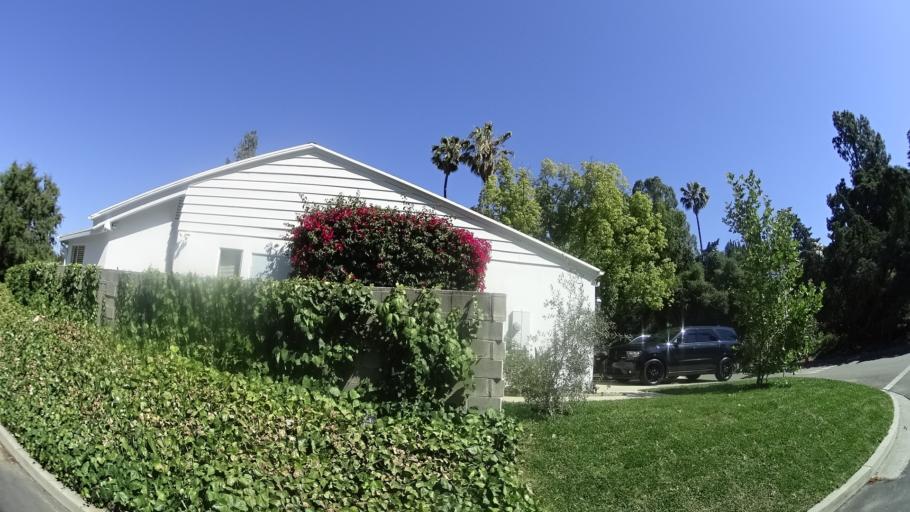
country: US
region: California
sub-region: Los Angeles County
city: Sherman Oaks
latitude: 34.1364
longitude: -118.4838
